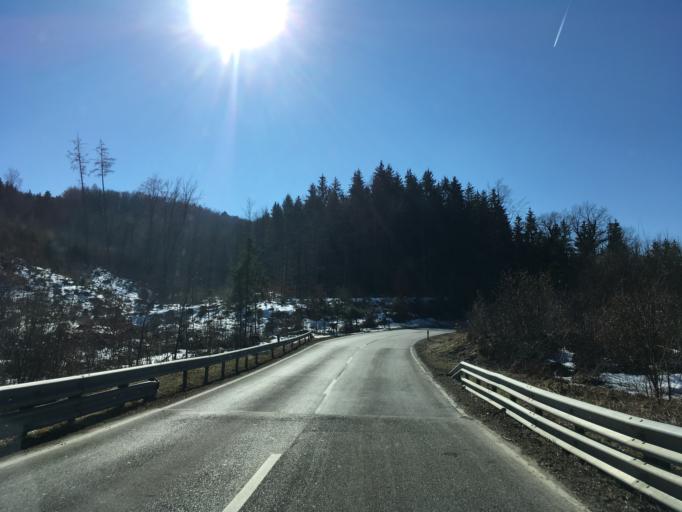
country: DE
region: Bavaria
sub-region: Upper Bavaria
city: Samerberg
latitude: 47.7933
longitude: 12.2003
